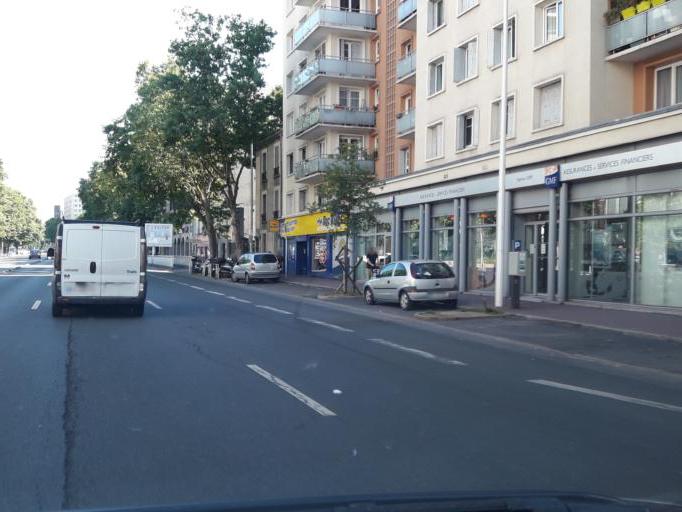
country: FR
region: Ile-de-France
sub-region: Departement des Hauts-de-Seine
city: Montrouge
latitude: 48.8160
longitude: 2.3256
